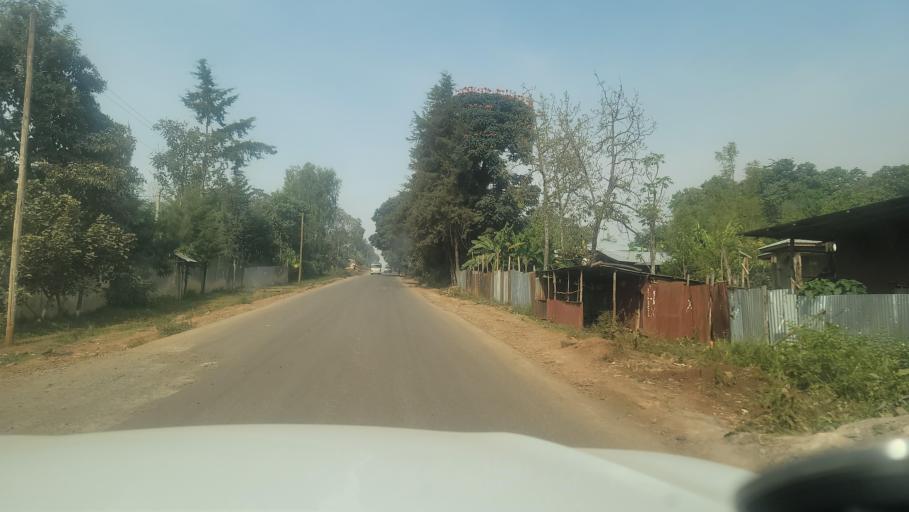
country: ET
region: Oromiya
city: Jima
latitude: 7.6996
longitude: 36.8127
